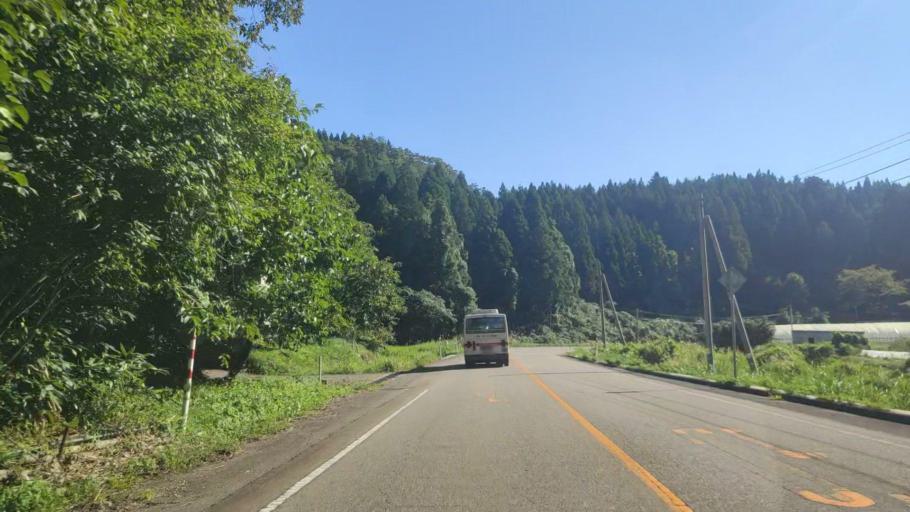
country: JP
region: Ishikawa
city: Nanao
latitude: 37.2429
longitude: 136.9880
